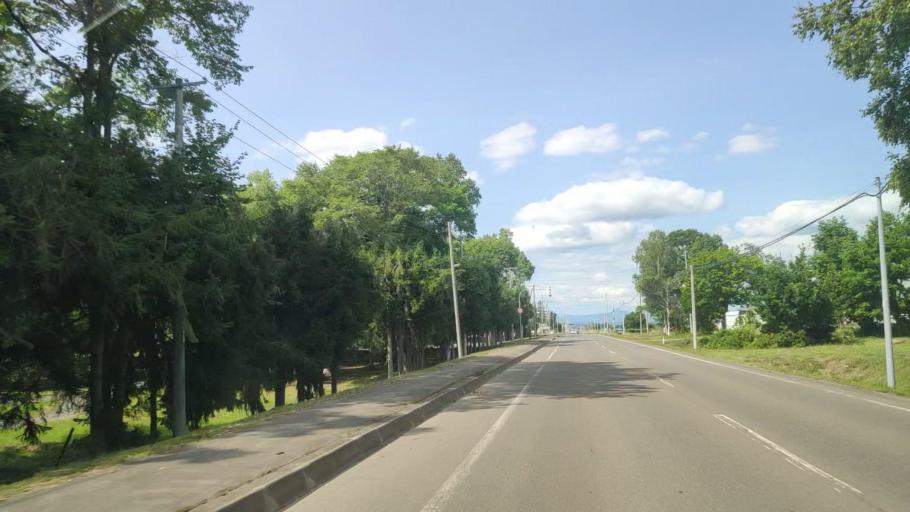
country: JP
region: Hokkaido
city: Nayoro
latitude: 44.2877
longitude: 142.4294
